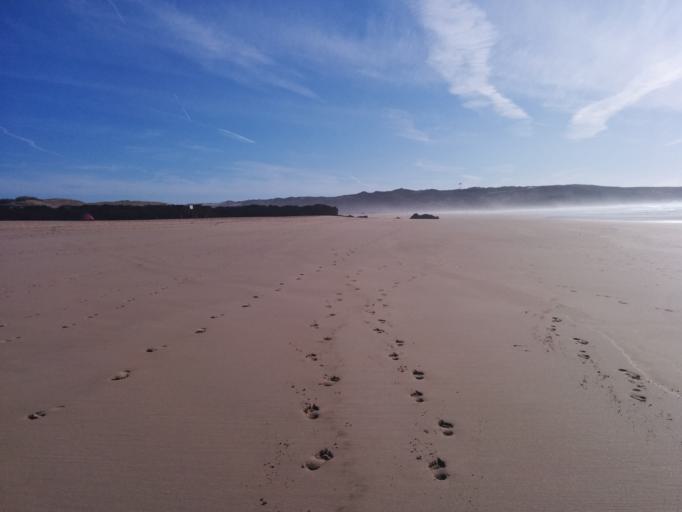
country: PT
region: Faro
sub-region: Vila do Bispo
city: Vila do Bispo
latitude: 37.2033
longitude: -8.8985
